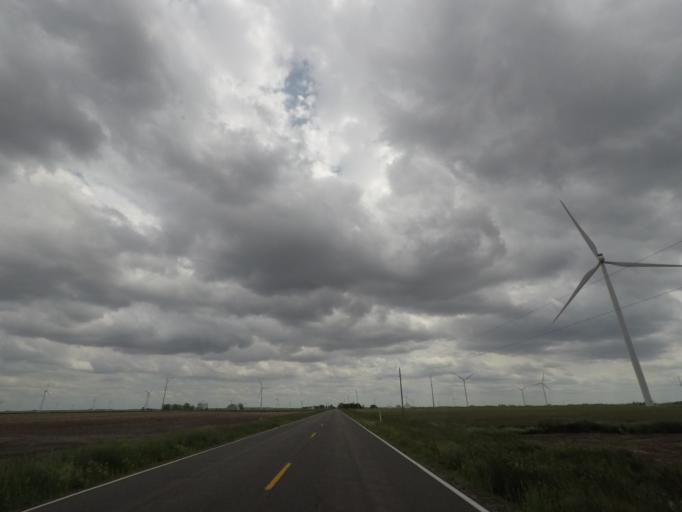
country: US
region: Illinois
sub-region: Macon County
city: Warrensburg
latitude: 40.0133
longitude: -89.0855
